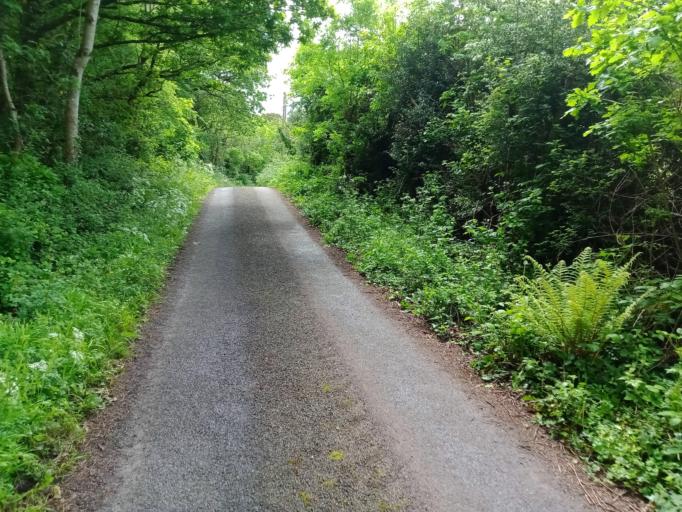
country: IE
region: Leinster
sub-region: Kilkenny
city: Thomastown
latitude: 52.5097
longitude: -7.1311
